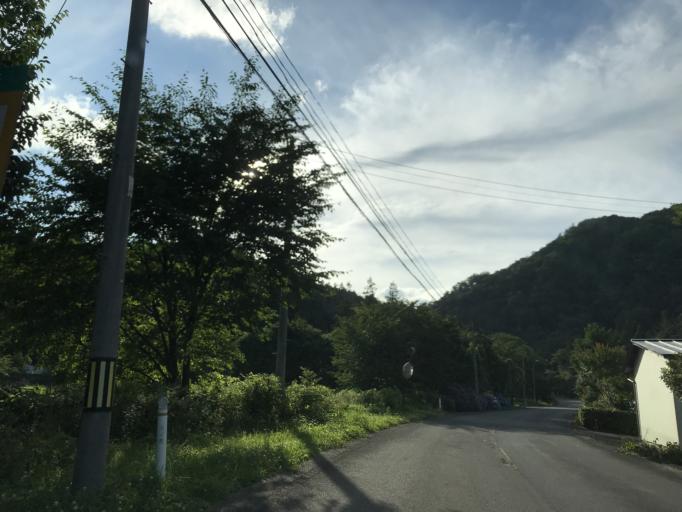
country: JP
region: Iwate
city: Ichinoseki
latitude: 38.9017
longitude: 140.9309
